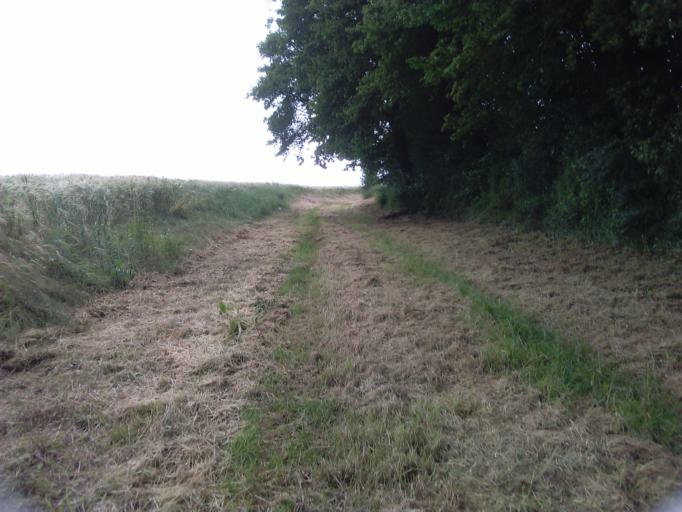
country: FR
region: Centre
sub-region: Departement du Cher
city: Sancerre
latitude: 47.3117
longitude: 2.7248
